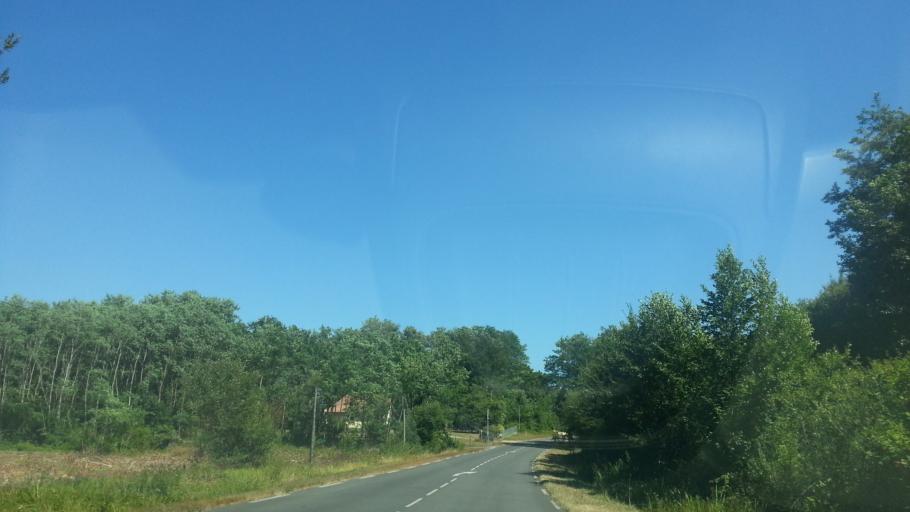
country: FR
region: Aquitaine
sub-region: Departement de la Gironde
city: Illats
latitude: 44.5625
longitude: -0.3679
